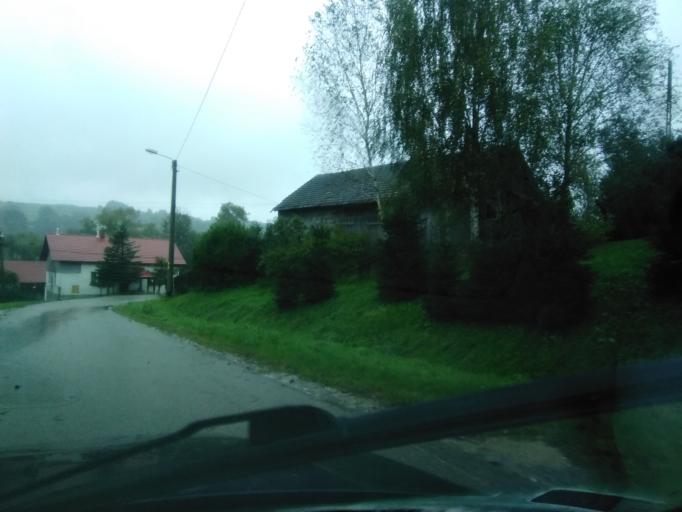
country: PL
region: Subcarpathian Voivodeship
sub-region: Powiat ropczycko-sedziszowski
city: Niedzwiada
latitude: 50.0150
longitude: 21.5461
